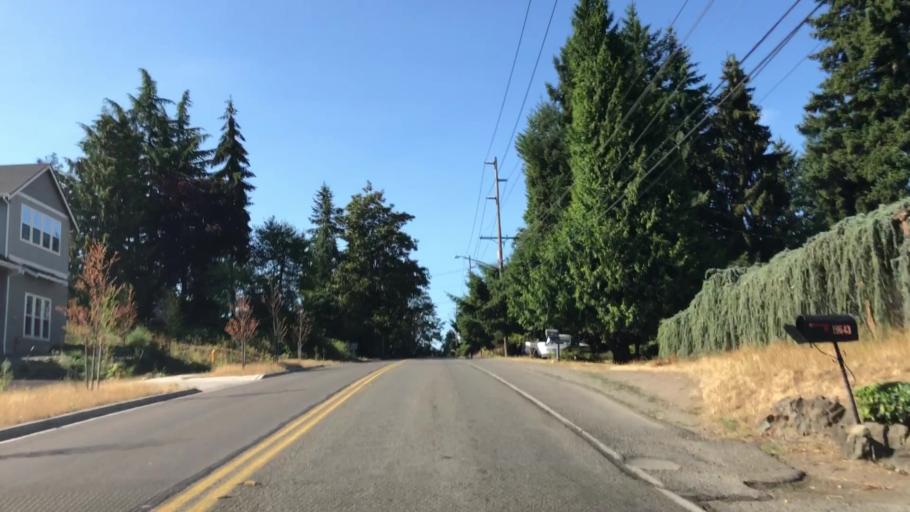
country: US
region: Washington
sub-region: King County
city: East Hill-Meridian
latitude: 47.4250
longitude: -122.2140
